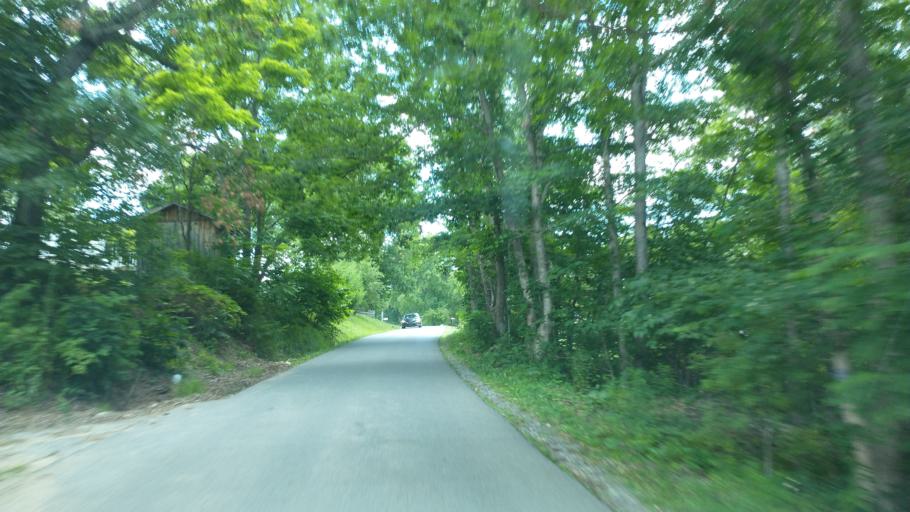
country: US
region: West Virginia
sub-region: Mercer County
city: Athens
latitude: 37.4603
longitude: -81.0534
